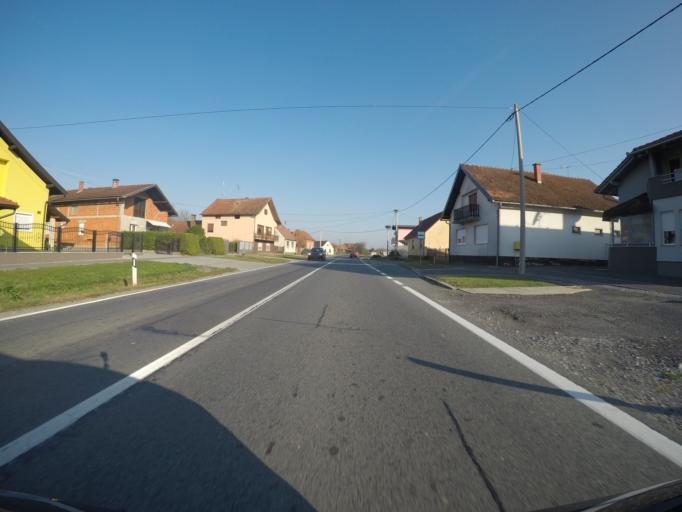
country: HR
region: Virovitick-Podravska
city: Pitomaca
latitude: 45.9685
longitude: 17.1953
